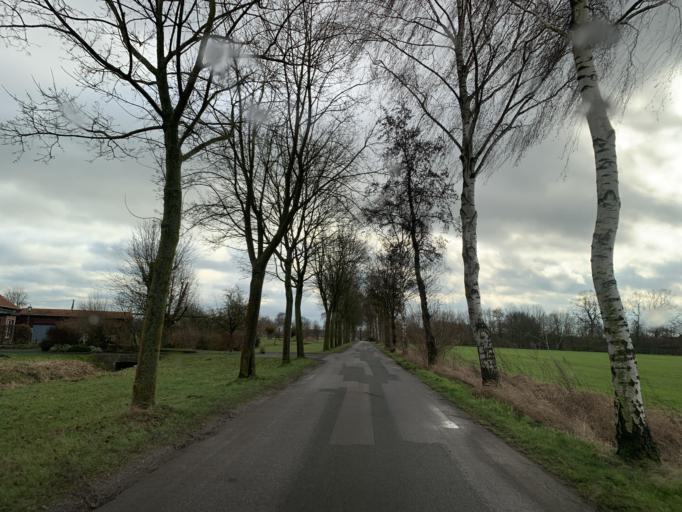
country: DE
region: North Rhine-Westphalia
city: Ludinghausen
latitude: 51.7724
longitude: 7.4783
